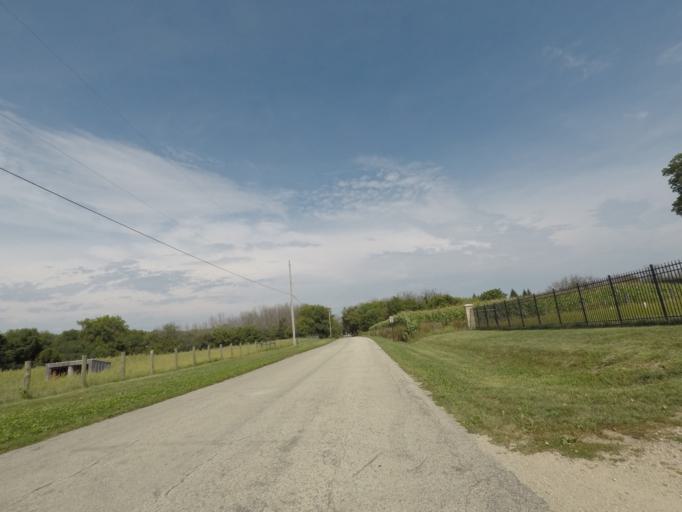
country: US
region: Wisconsin
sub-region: Jefferson County
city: Lake Koshkonong
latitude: 42.8960
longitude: -88.8741
